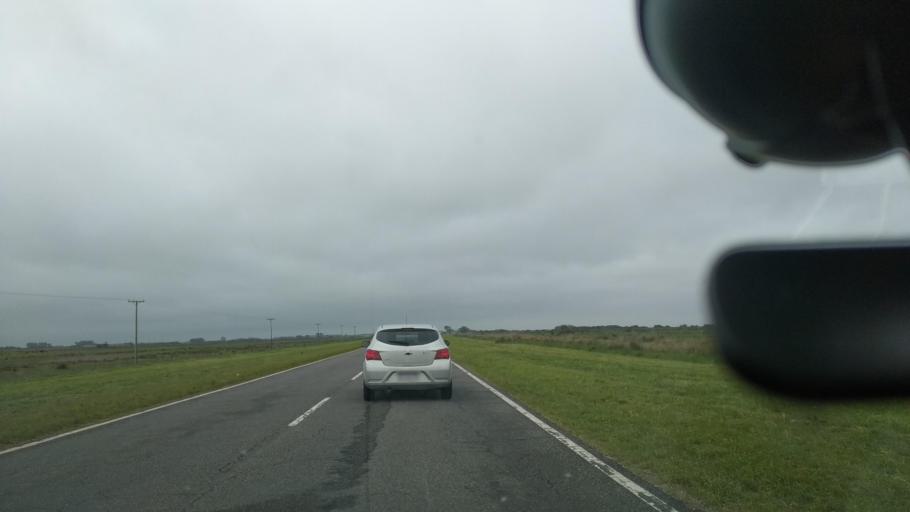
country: AR
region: Buenos Aires
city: Veronica
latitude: -35.6062
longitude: -57.2810
